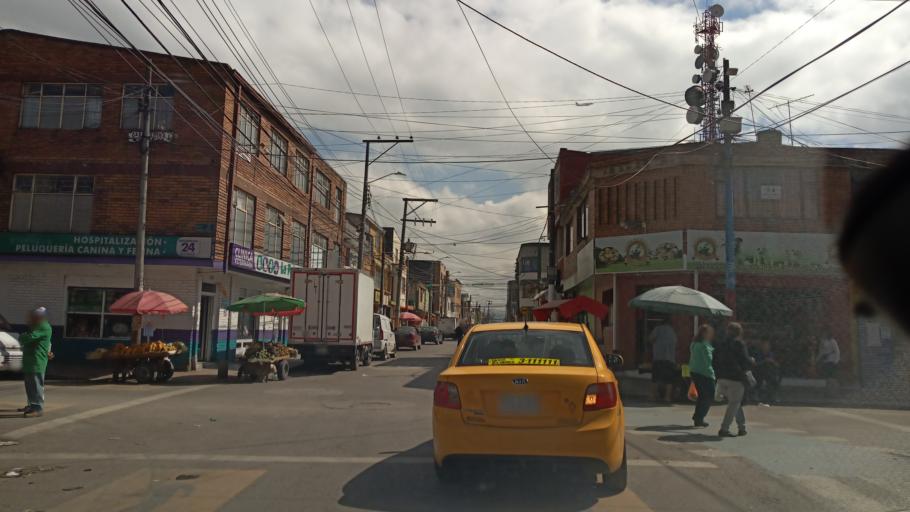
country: CO
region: Cundinamarca
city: Funza
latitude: 4.6765
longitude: -74.1444
